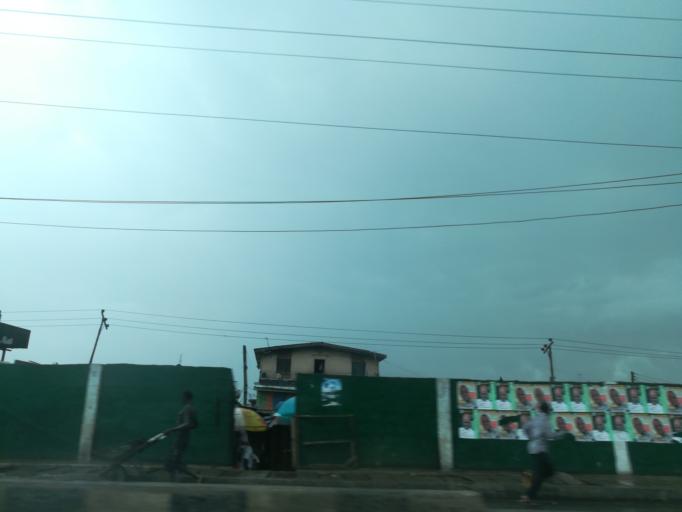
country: NG
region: Lagos
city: Ojota
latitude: 6.5991
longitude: 3.3874
